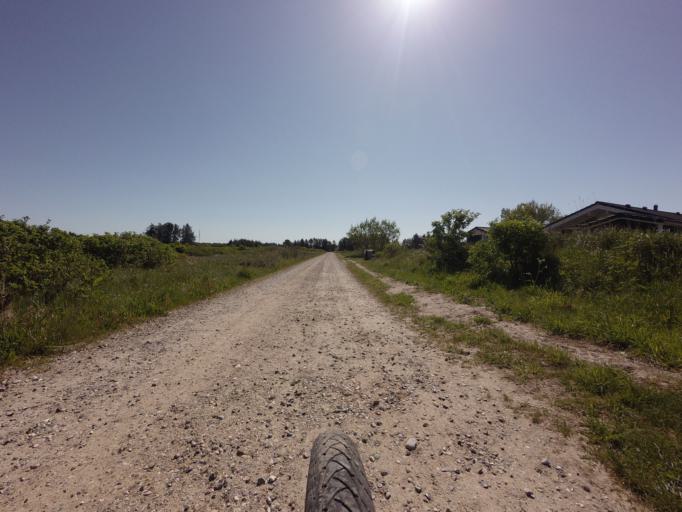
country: DK
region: North Denmark
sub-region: Jammerbugt Kommune
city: Pandrup
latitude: 57.3169
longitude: 9.6668
